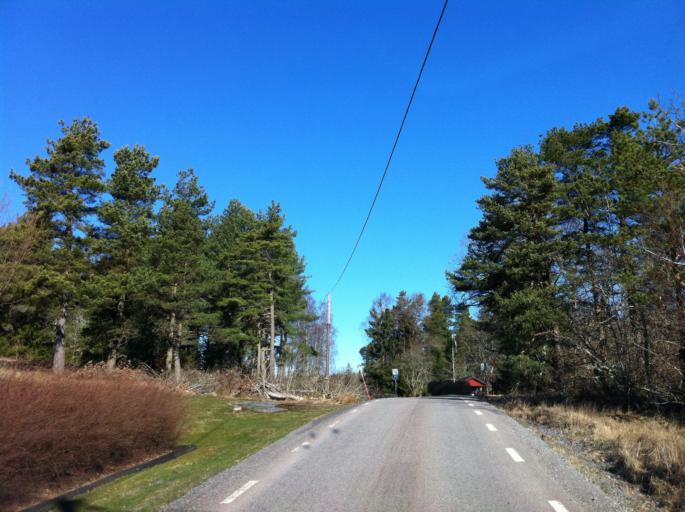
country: SE
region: Vaestra Goetaland
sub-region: Grastorps Kommun
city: Graestorp
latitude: 58.4441
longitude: 12.6118
